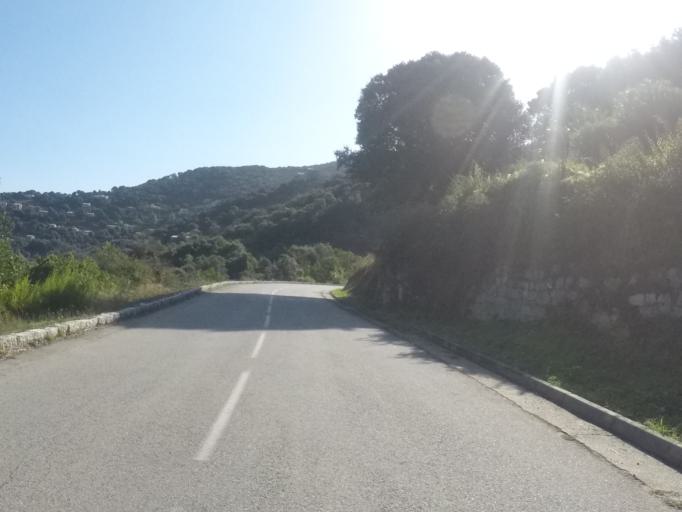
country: FR
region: Corsica
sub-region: Departement de la Corse-du-Sud
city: Olmeto
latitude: 41.7455
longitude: 8.9037
